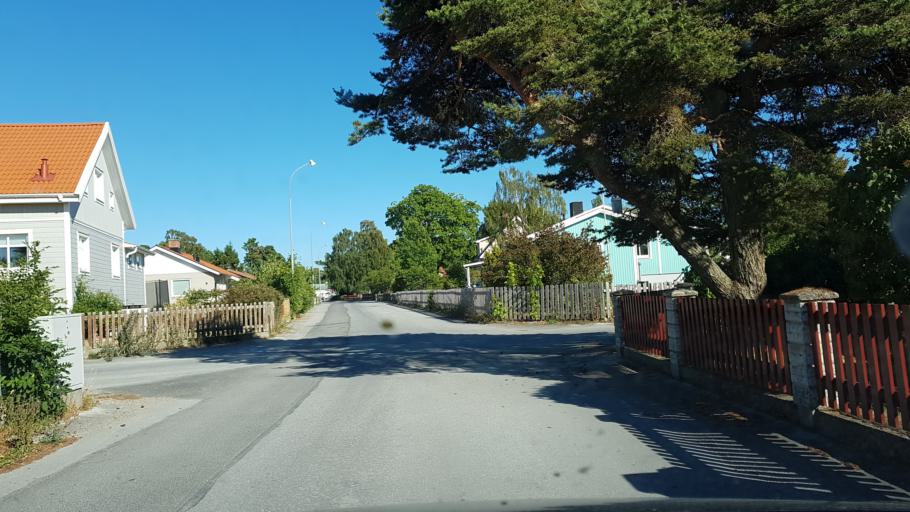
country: SE
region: Gotland
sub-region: Gotland
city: Vibble
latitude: 57.6022
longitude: 18.2467
